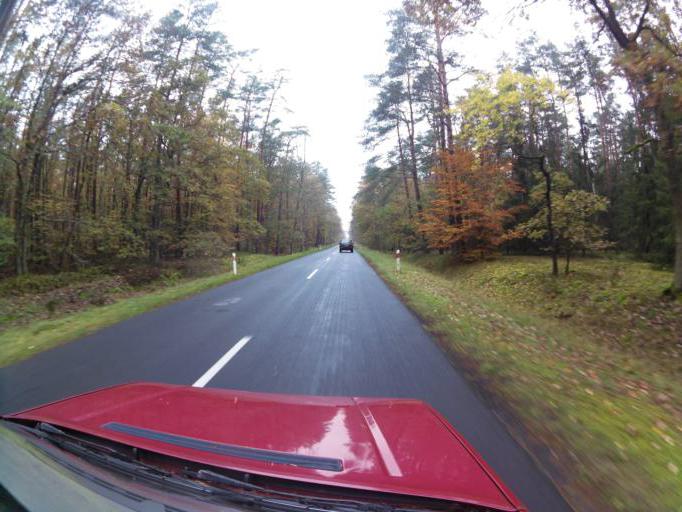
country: PL
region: West Pomeranian Voivodeship
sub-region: Powiat policki
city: Dobra
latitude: 53.5624
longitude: 14.4456
